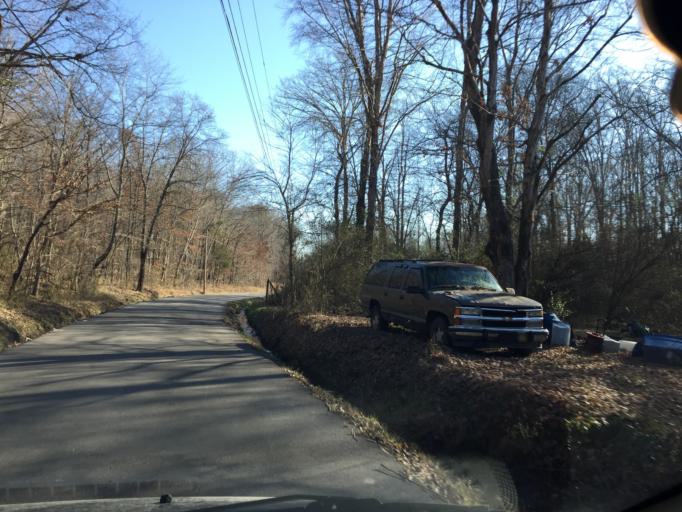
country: US
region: Tennessee
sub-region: Hamilton County
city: Collegedale
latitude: 35.0790
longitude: -85.0873
